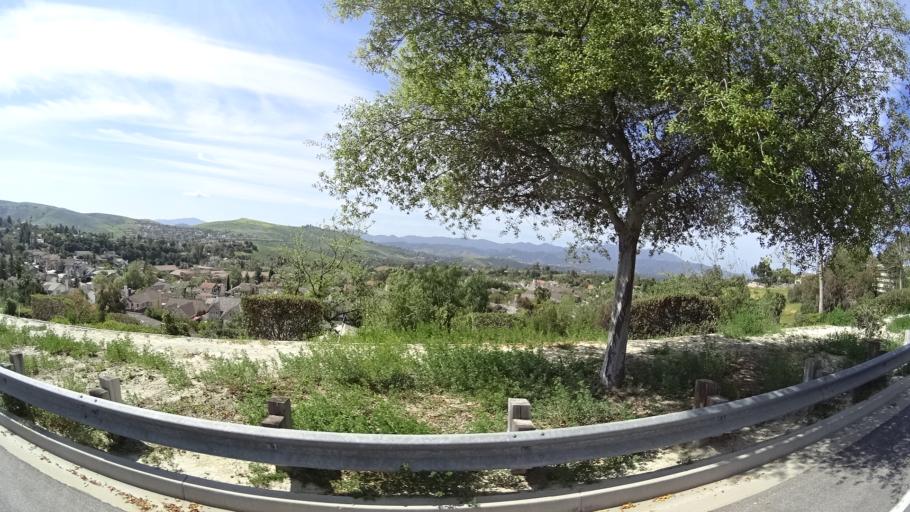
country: US
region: California
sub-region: Ventura County
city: Thousand Oaks
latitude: 34.2232
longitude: -118.8344
